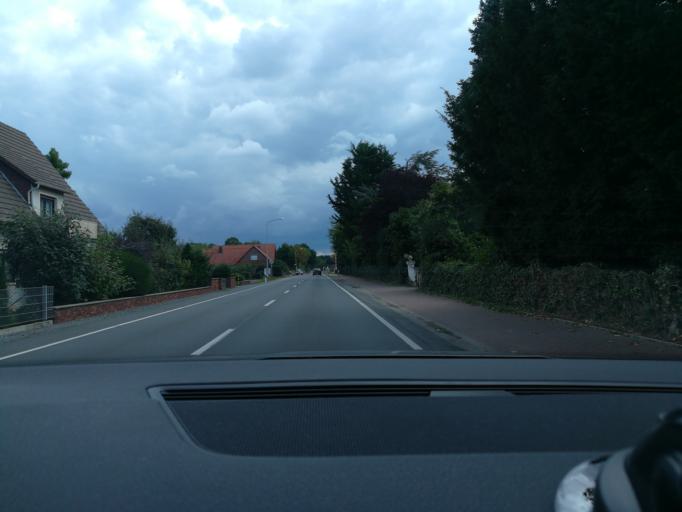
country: DE
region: North Rhine-Westphalia
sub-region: Regierungsbezirk Detmold
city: Minden
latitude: 52.3208
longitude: 8.8737
